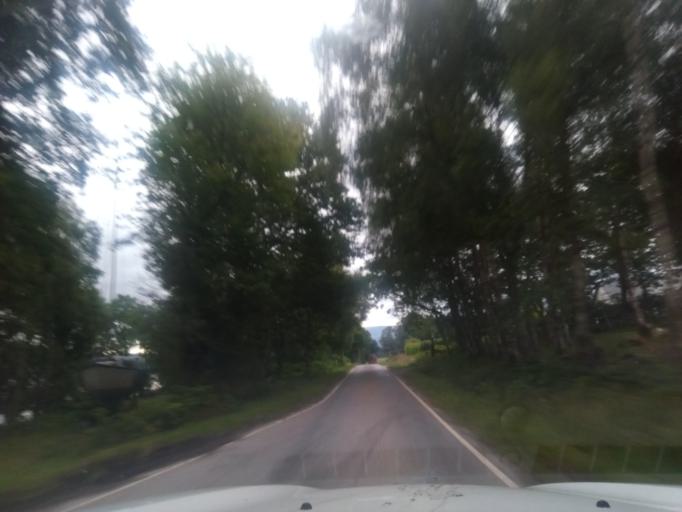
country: GB
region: Scotland
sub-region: Highland
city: Fort William
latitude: 56.8453
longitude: -5.2768
